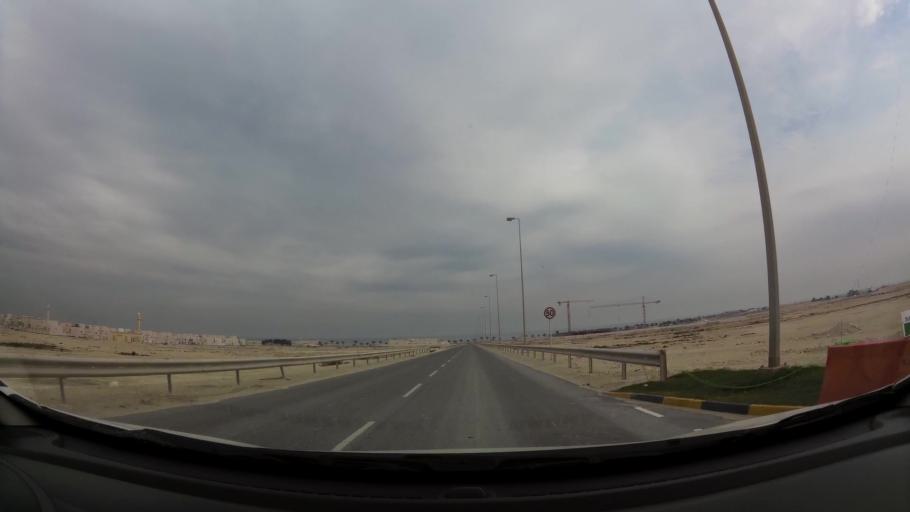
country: BH
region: Northern
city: Ar Rifa'
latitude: 26.0483
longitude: 50.6138
